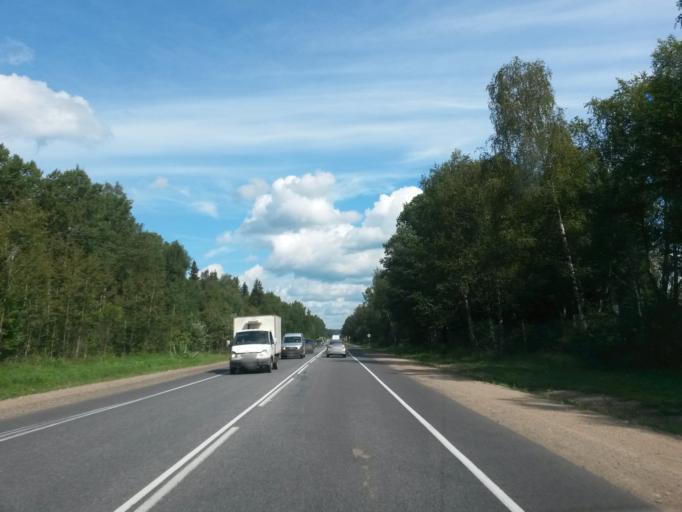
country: RU
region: Jaroslavl
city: Pereslavl'-Zalesskiy
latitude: 56.8231
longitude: 38.9076
